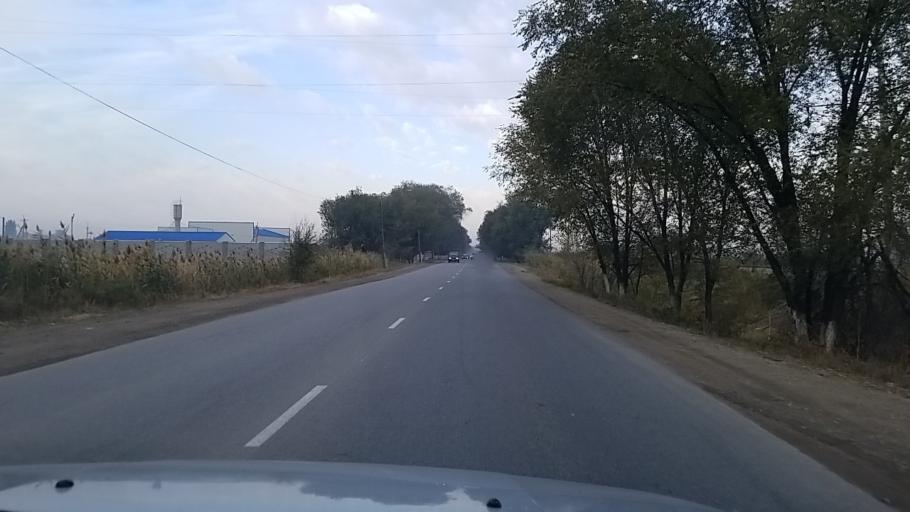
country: KZ
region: Almaty Oblysy
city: Burunday
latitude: 43.3580
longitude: 76.7797
